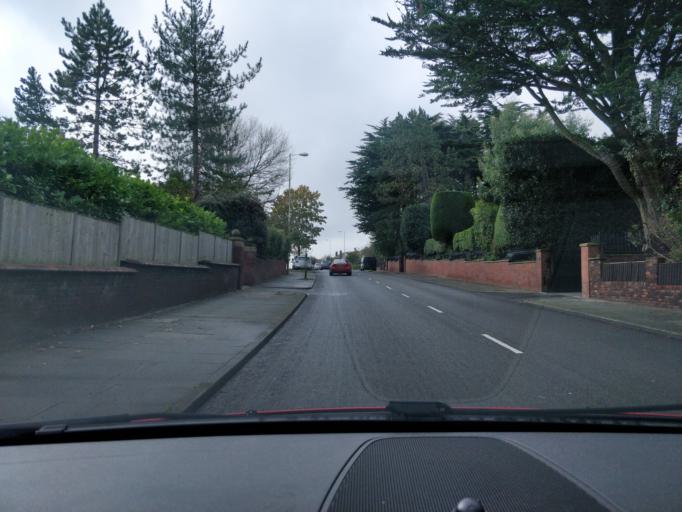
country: GB
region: England
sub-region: Sefton
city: Southport
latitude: 53.6296
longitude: -3.0264
